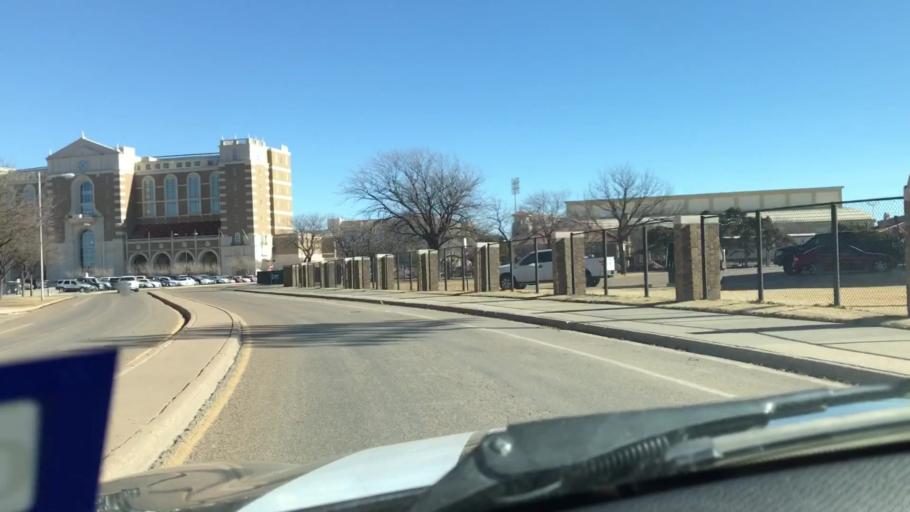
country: US
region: Texas
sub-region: Lubbock County
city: Lubbock
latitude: 33.5894
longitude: -101.8768
